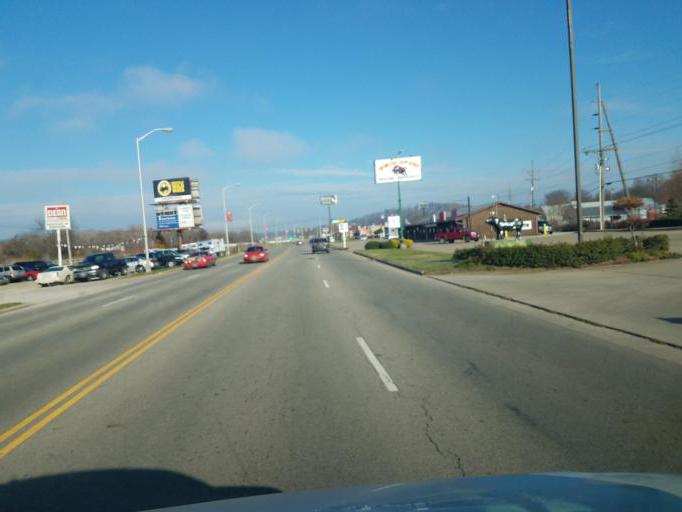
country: US
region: Ohio
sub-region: Scioto County
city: Wheelersburg
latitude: 38.7213
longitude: -82.8589
